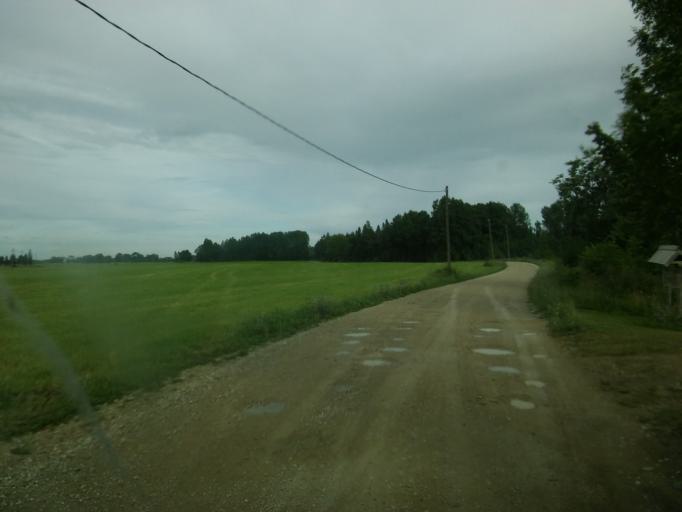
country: EE
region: Raplamaa
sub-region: Rapla vald
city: Rapla
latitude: 58.9024
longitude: 24.7481
